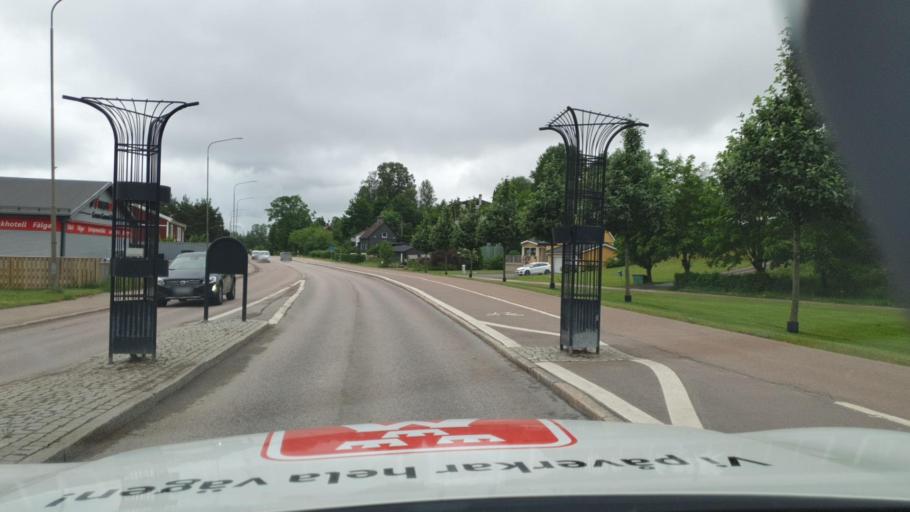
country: SE
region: Vaermland
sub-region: Grums Kommun
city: Grums
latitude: 59.3612
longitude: 13.1116
